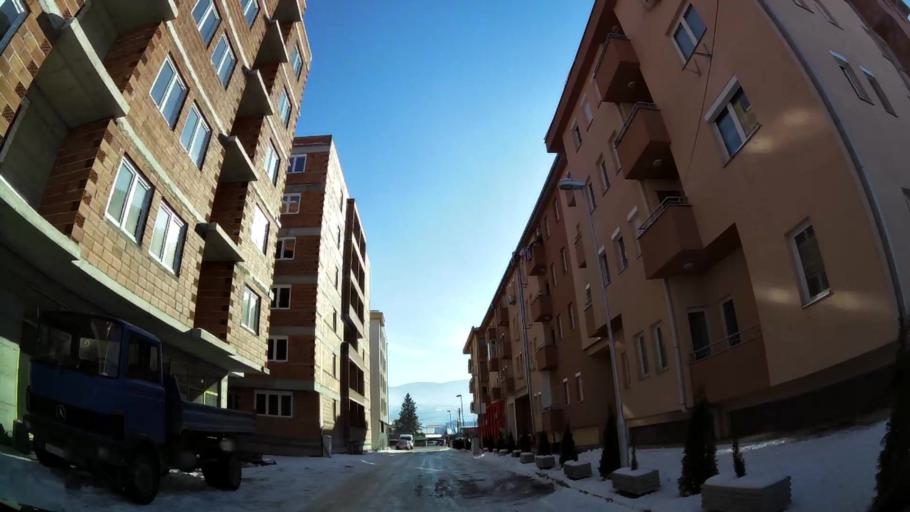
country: MK
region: Saraj
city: Saraj
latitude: 42.0014
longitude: 21.3290
